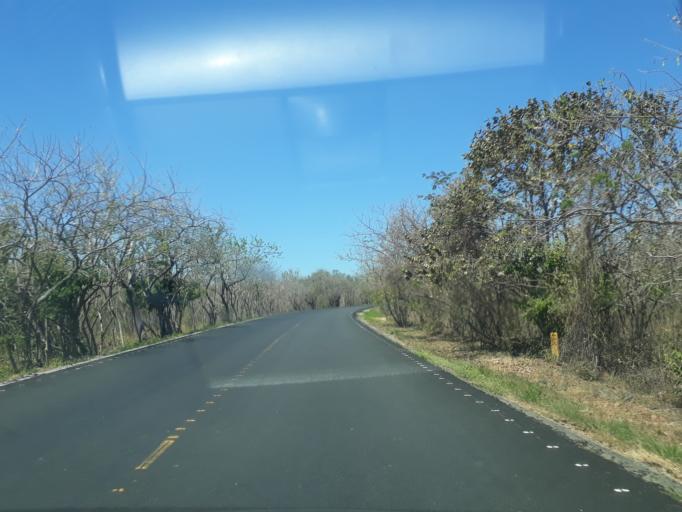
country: CR
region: Guanacaste
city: La Cruz
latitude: 10.9392
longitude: -85.6115
